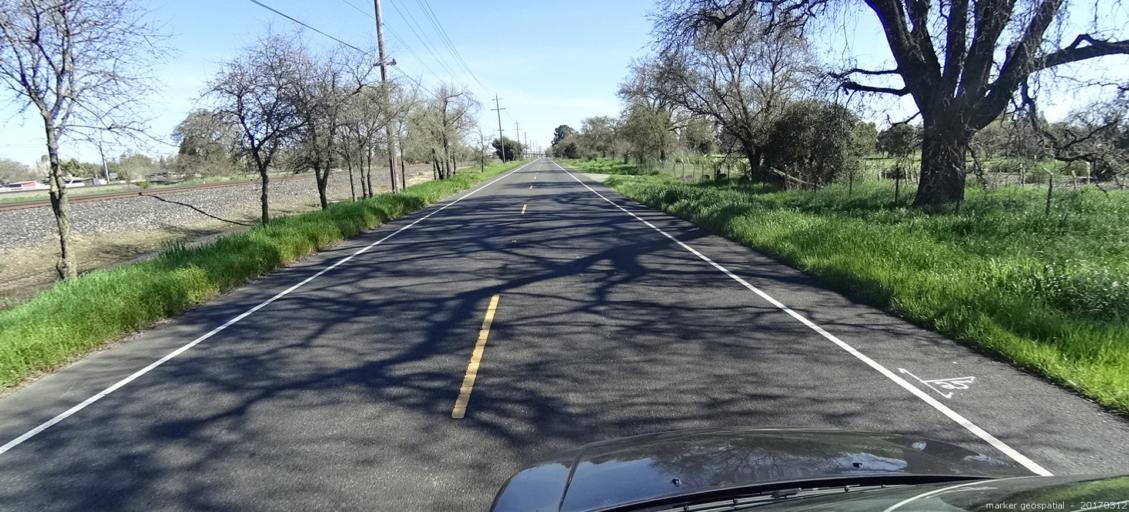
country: US
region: California
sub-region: Sacramento County
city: Arden-Arcade
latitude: 38.6271
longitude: -121.4174
